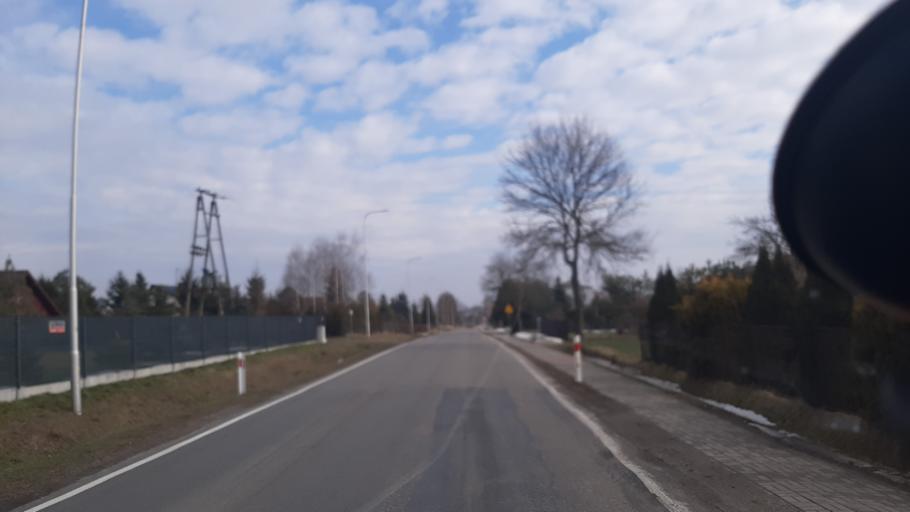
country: PL
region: Lublin Voivodeship
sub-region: Powiat lubelski
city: Niemce
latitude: 51.3617
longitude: 22.5822
